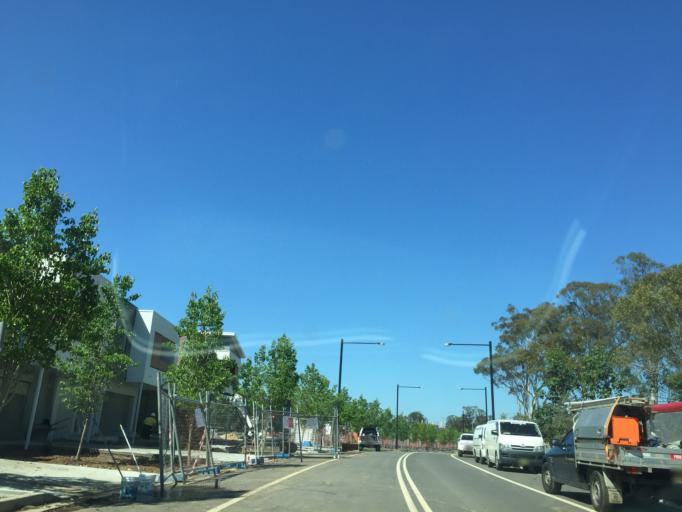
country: AU
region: New South Wales
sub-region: Blacktown
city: Blacktown
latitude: -33.7609
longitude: 150.9024
